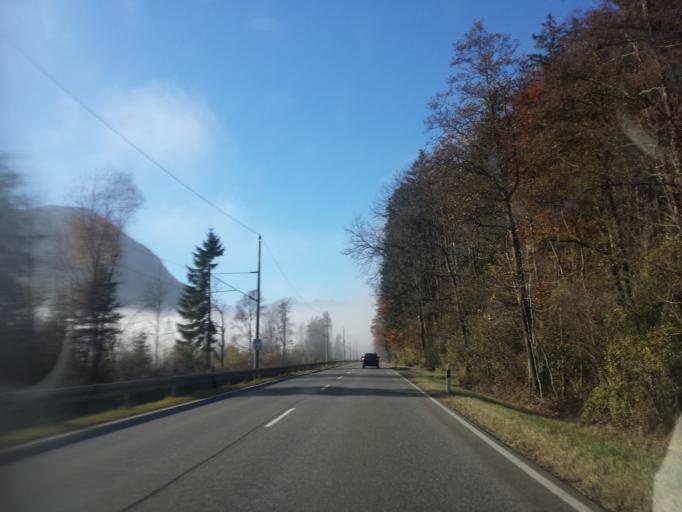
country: DE
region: Bavaria
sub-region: Upper Bavaria
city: Eschenlohe
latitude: 47.5803
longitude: 11.1671
